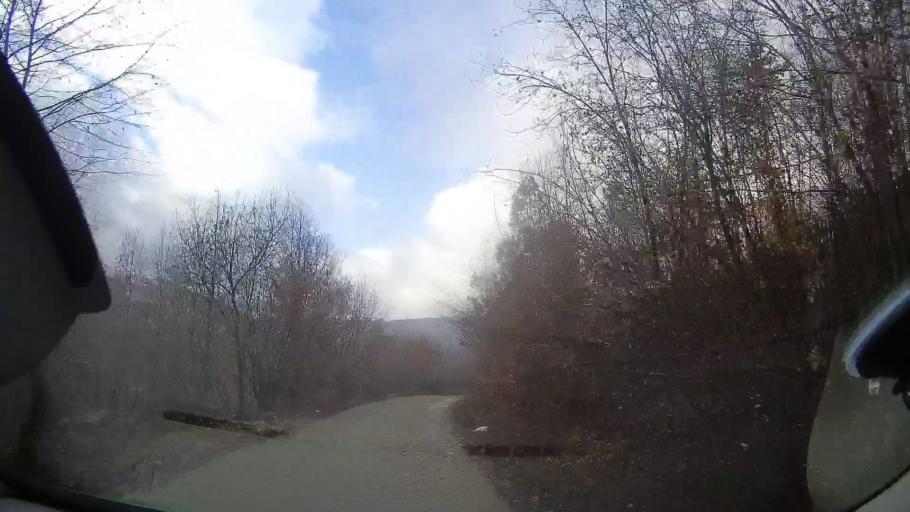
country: RO
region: Cluj
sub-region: Comuna Valea Ierii
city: Valea Ierii
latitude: 46.6783
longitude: 23.3136
